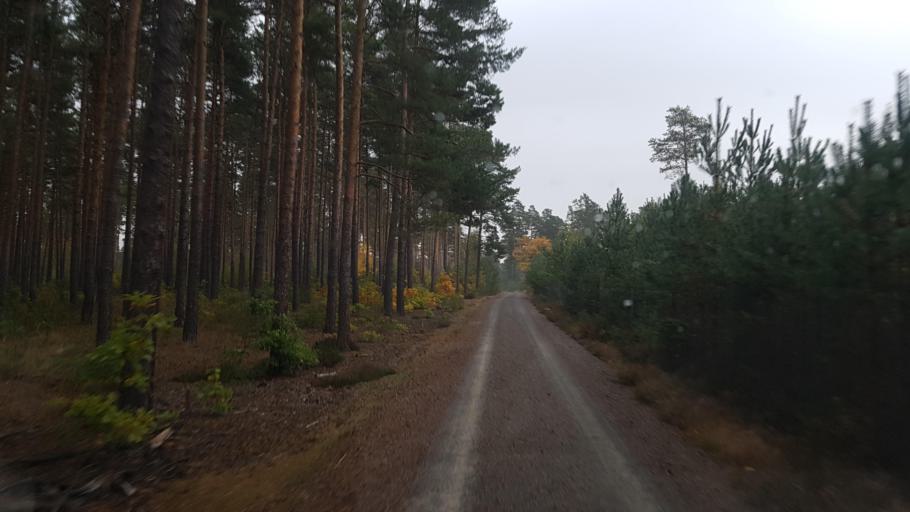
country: DE
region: Brandenburg
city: Lebusa
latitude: 51.7609
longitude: 13.4104
